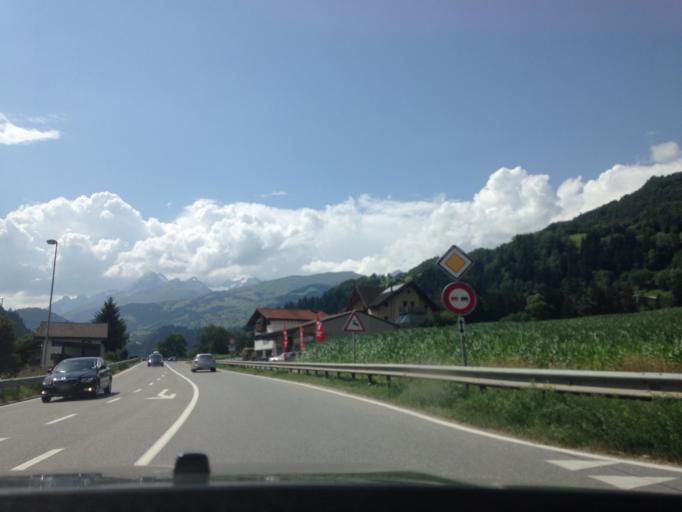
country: CH
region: Grisons
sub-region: Surselva District
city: Ilanz
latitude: 46.7748
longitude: 9.1775
